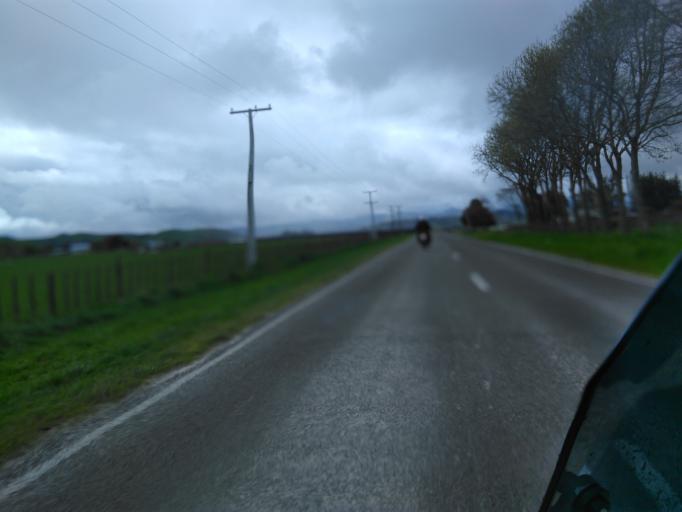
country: NZ
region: Gisborne
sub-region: Gisborne District
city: Gisborne
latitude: -38.6467
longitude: 177.8514
